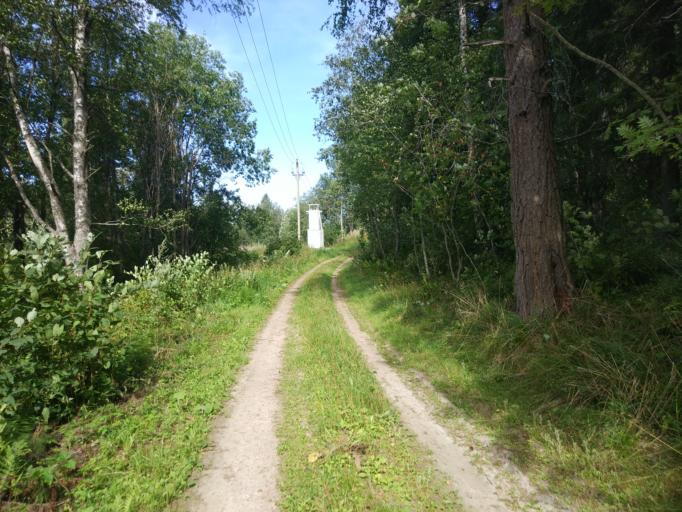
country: RU
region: Leningrad
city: Kamennogorsk
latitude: 61.0476
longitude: 29.4669
